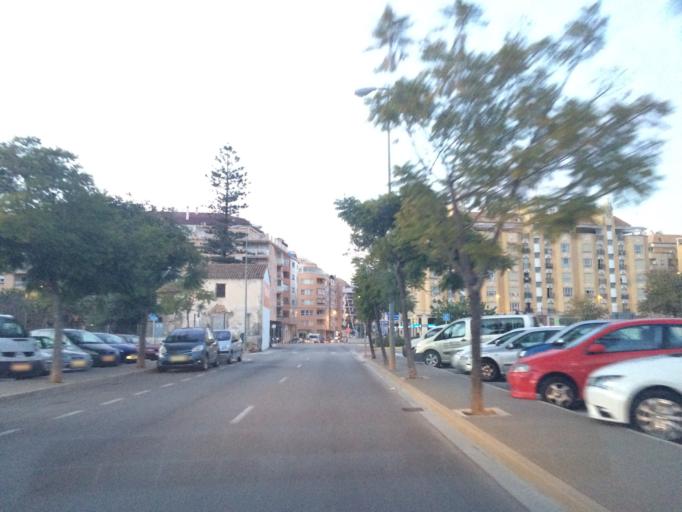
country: ES
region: Valencia
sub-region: Provincia de Alicante
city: Denia
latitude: 38.8350
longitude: 0.1096
